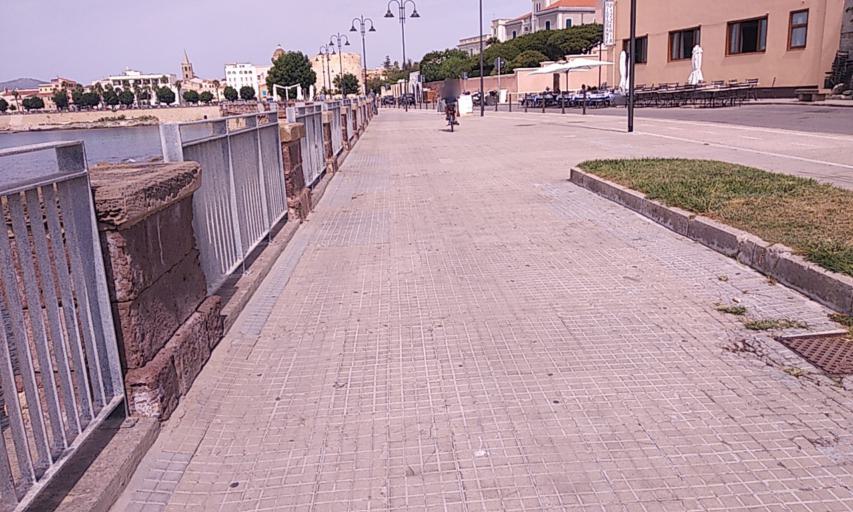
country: IT
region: Sardinia
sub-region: Provincia di Sassari
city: Alghero
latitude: 40.5535
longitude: 8.3161
